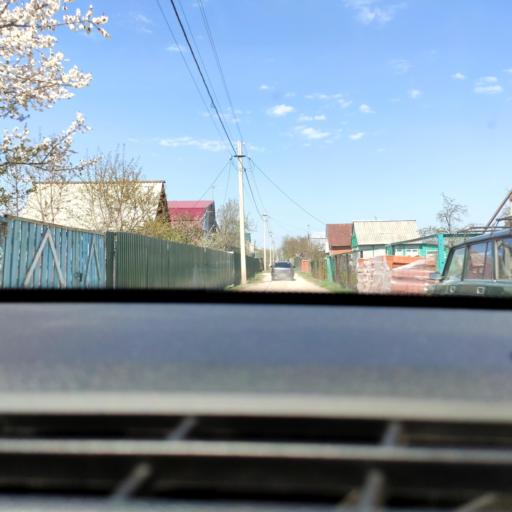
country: RU
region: Samara
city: Tol'yatti
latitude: 53.5935
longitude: 49.3008
